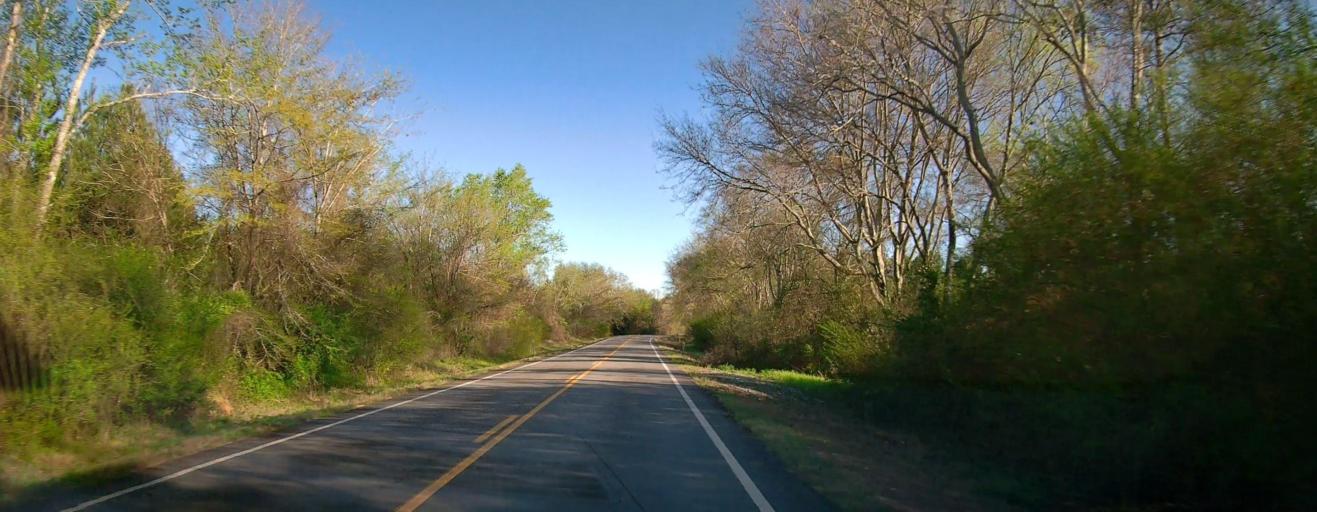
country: US
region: Georgia
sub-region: Baldwin County
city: Hardwick
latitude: 32.9576
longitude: -83.1679
